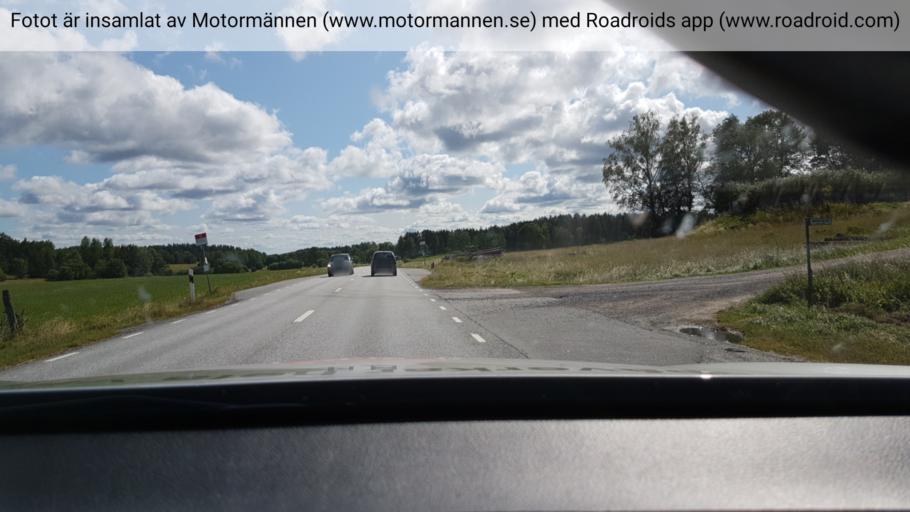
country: SE
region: Stockholm
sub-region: Norrtalje Kommun
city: Norrtalje
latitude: 59.9092
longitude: 18.7046
